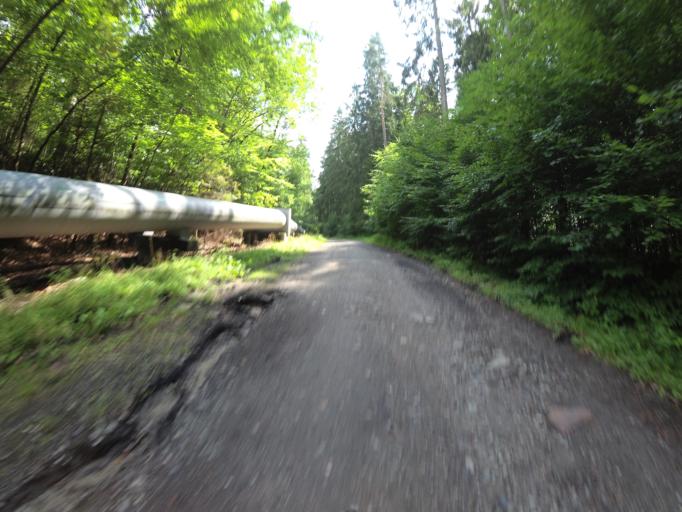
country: PL
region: Pomeranian Voivodeship
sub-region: Gdynia
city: Wielki Kack
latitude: 54.5103
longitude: 18.4863
